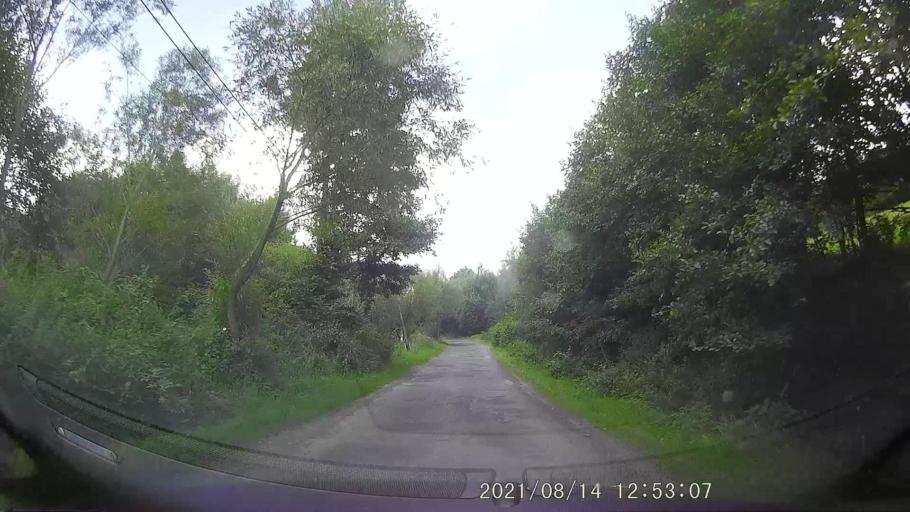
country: PL
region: Lower Silesian Voivodeship
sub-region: Powiat klodzki
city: Stronie Slaskie
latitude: 50.3198
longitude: 16.8272
